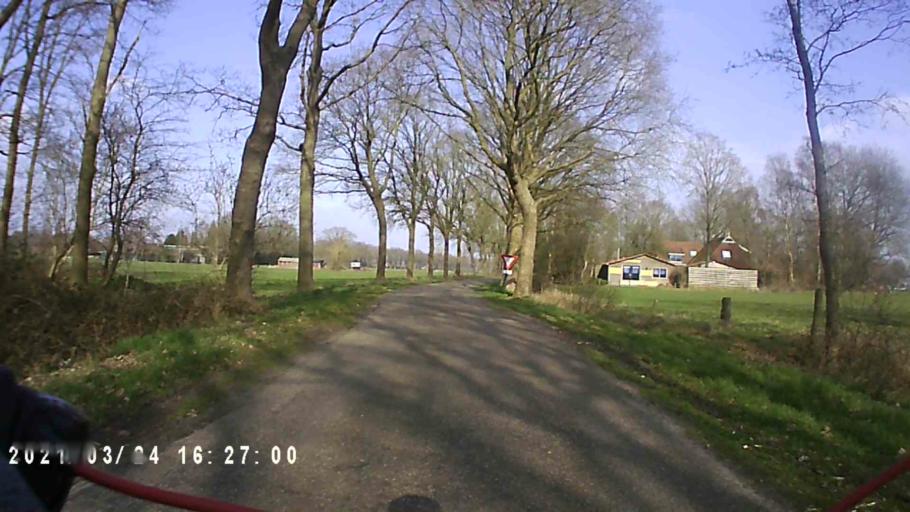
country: NL
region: Groningen
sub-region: Gemeente Leek
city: Leek
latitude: 53.0652
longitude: 6.2711
